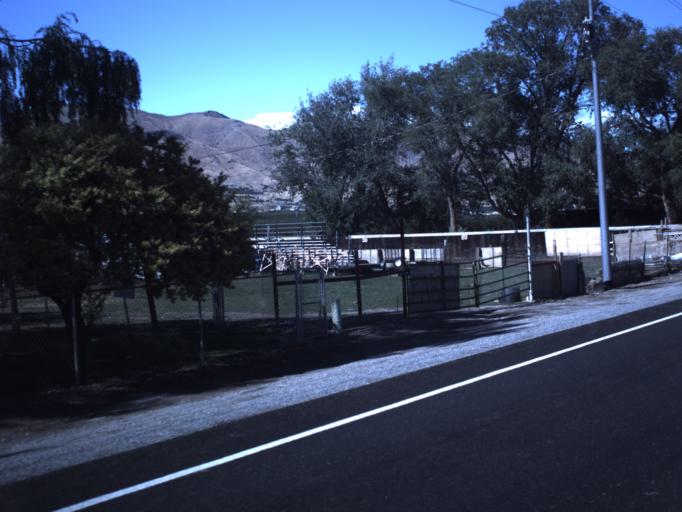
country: US
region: Utah
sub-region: Utah County
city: West Mountain
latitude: 40.0294
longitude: -111.7871
